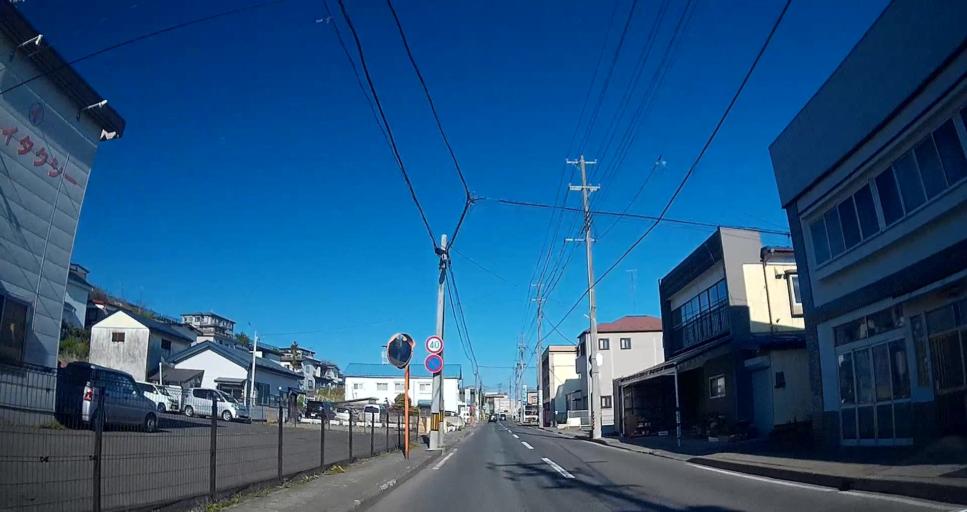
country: JP
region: Aomori
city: Hachinohe
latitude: 40.5236
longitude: 141.5328
